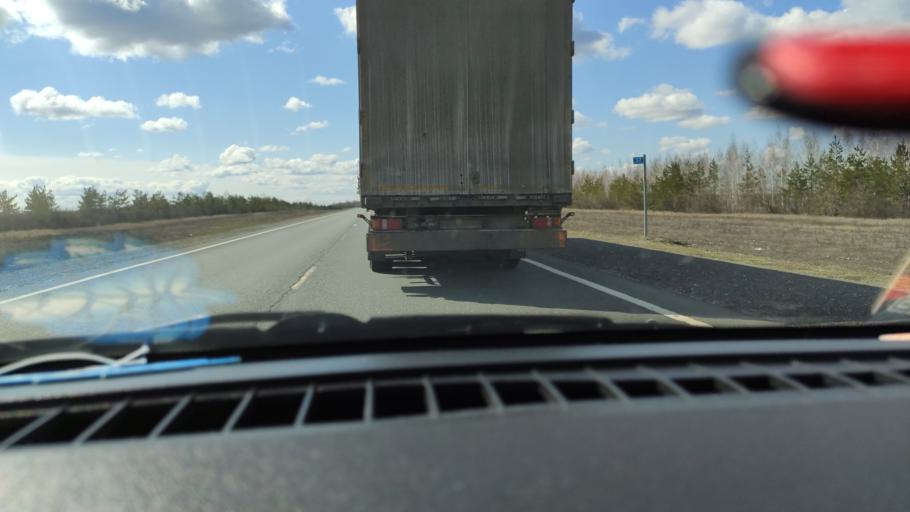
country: RU
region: Samara
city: Syzran'
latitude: 52.8784
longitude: 48.2906
